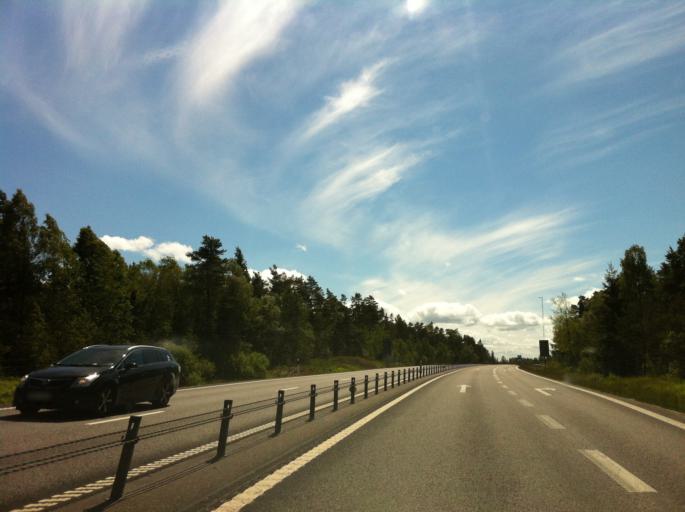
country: SE
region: Vaestra Goetaland
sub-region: Vanersborgs Kommun
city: Vanersborg
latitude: 58.3984
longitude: 12.2967
